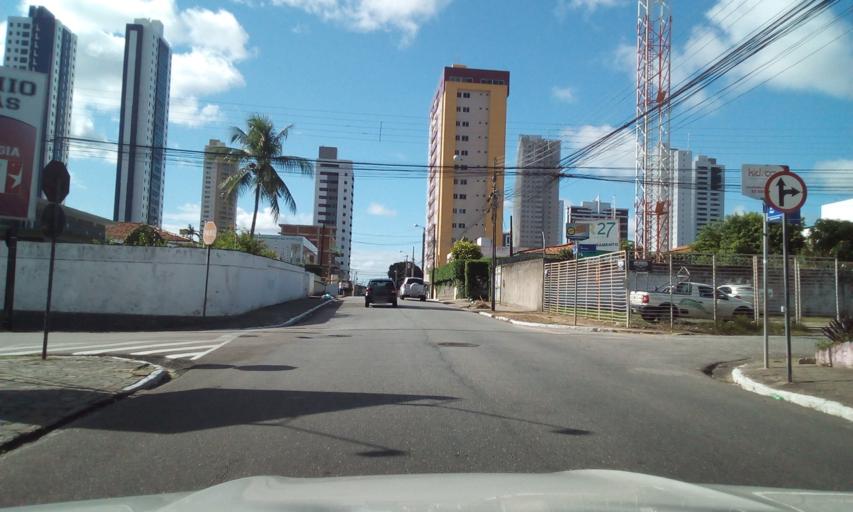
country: BR
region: Paraiba
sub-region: Joao Pessoa
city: Joao Pessoa
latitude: -7.1178
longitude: -34.8534
